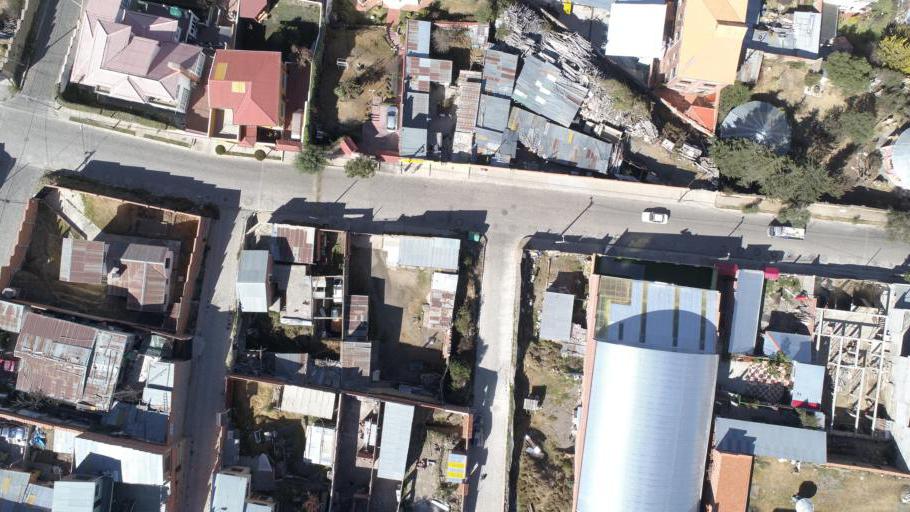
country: BO
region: La Paz
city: La Paz
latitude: -16.5414
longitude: -68.0536
